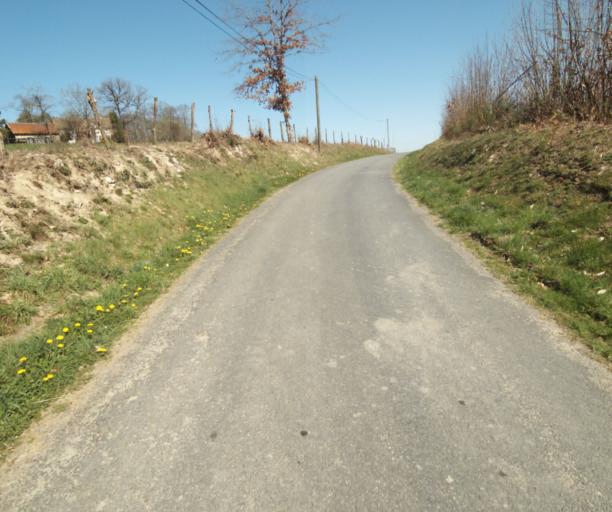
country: FR
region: Limousin
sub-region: Departement de la Correze
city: Saint-Mexant
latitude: 45.2906
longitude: 1.6414
